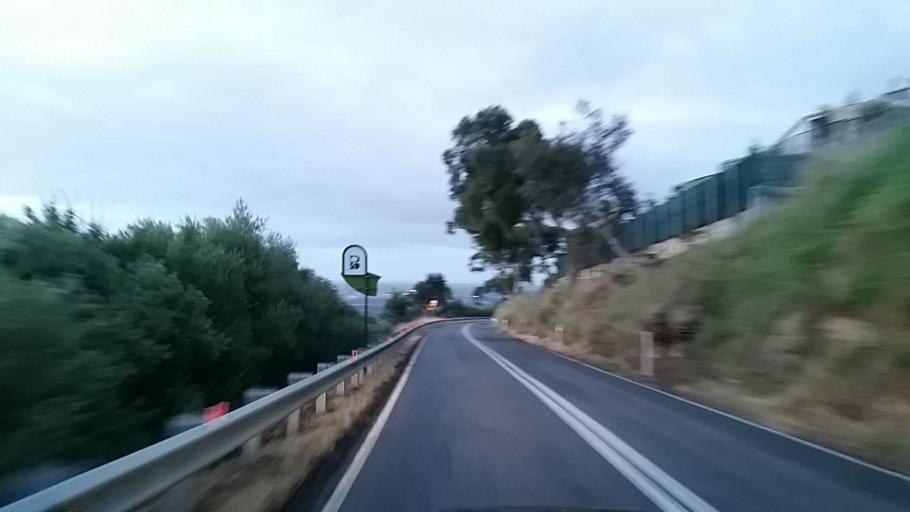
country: AU
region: South Australia
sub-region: Burnside
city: Beaumont
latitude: -34.9467
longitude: 138.6721
